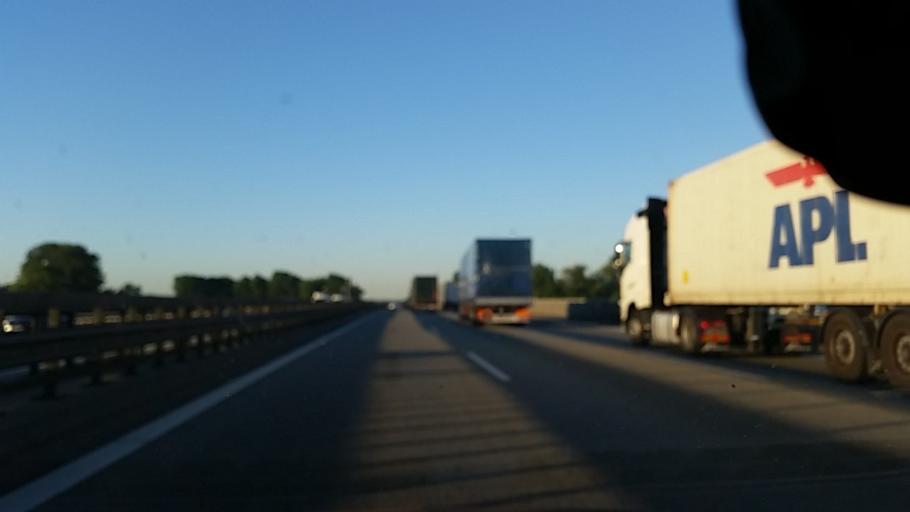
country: DE
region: Hamburg
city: Harburg
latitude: 53.4753
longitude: 10.0227
